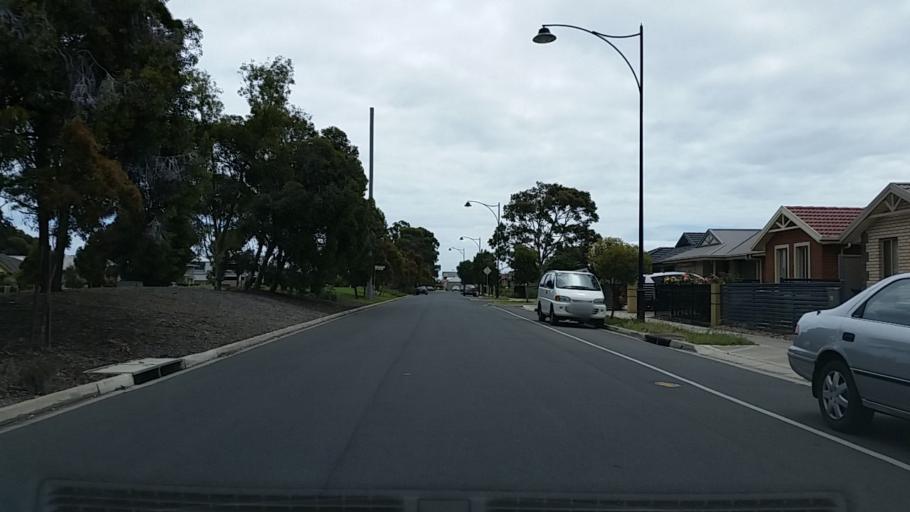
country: AU
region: South Australia
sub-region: Charles Sturt
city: Woodville North
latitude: -34.8560
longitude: 138.5521
